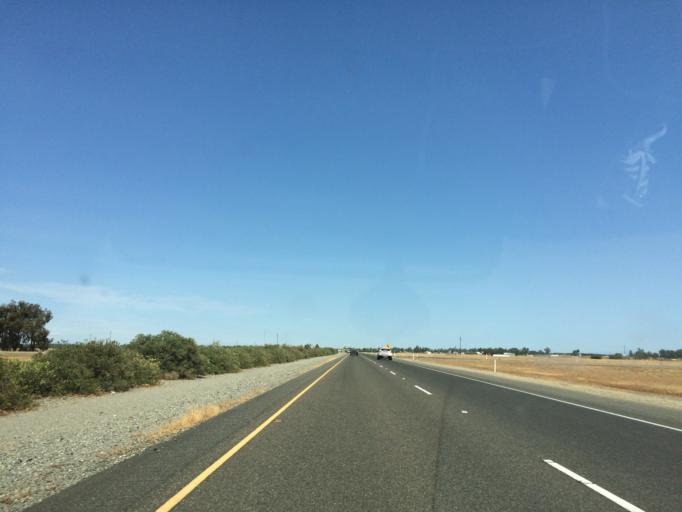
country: US
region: California
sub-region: Glenn County
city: Orland
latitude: 39.6825
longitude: -122.2046
